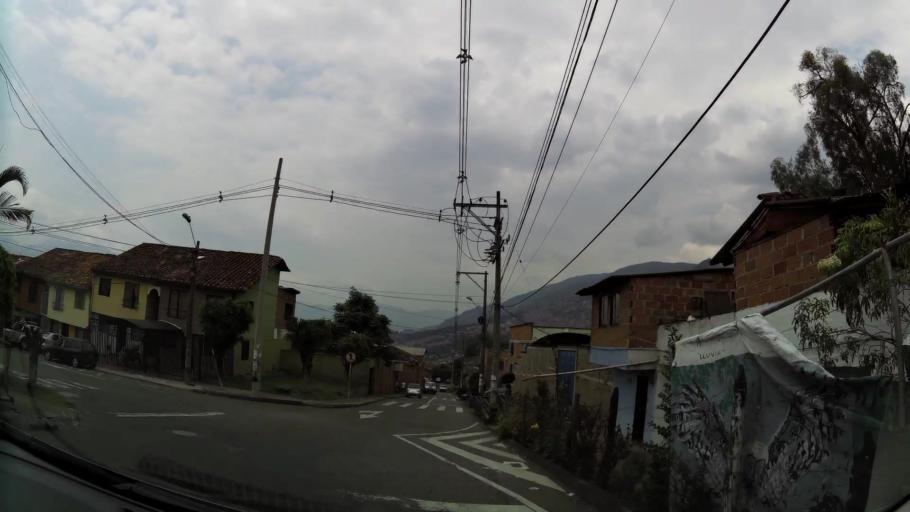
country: CO
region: Antioquia
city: Medellin
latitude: 6.2313
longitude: -75.5489
